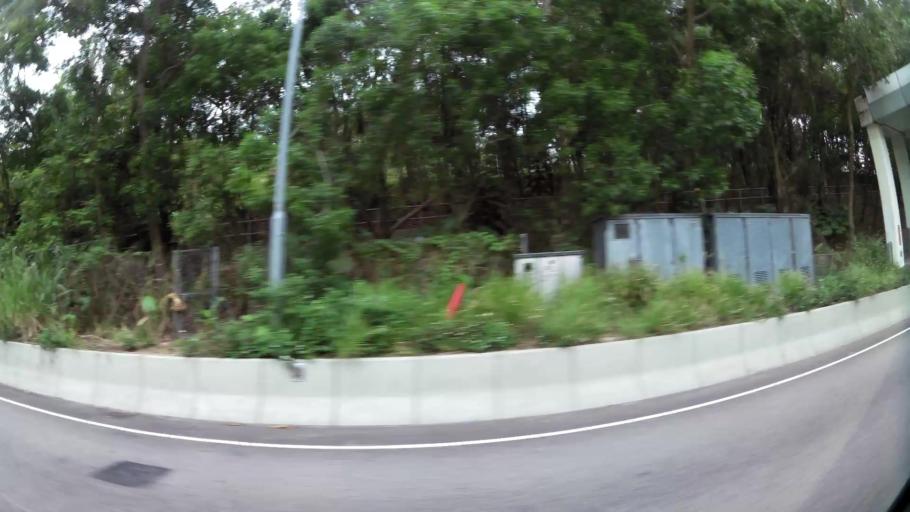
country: HK
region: Tsuen Wan
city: Tsuen Wan
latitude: 22.3759
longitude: 114.1168
